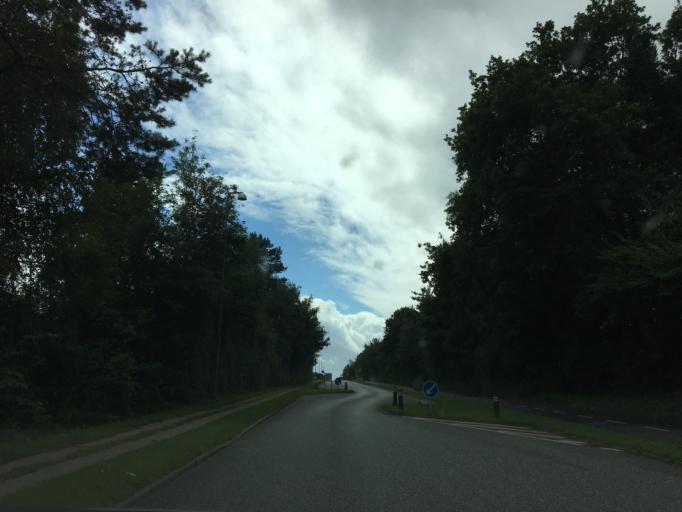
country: DK
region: South Denmark
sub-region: Vejle Kommune
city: Vejle
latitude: 55.7215
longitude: 9.5964
